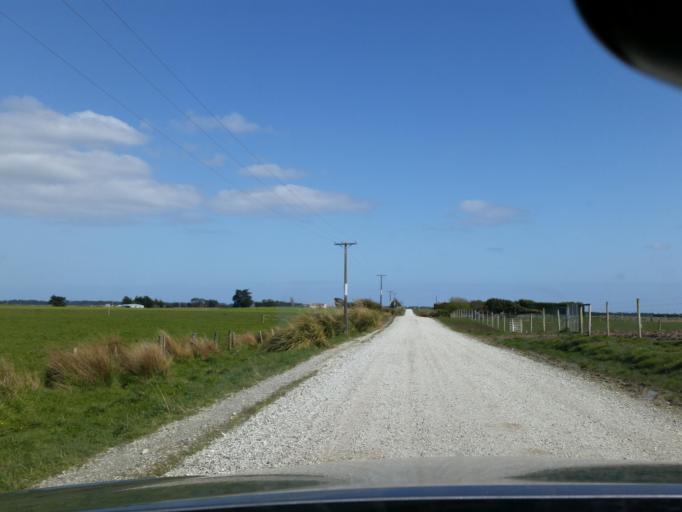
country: NZ
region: Southland
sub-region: Invercargill City
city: Invercargill
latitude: -46.4426
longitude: 168.5062
